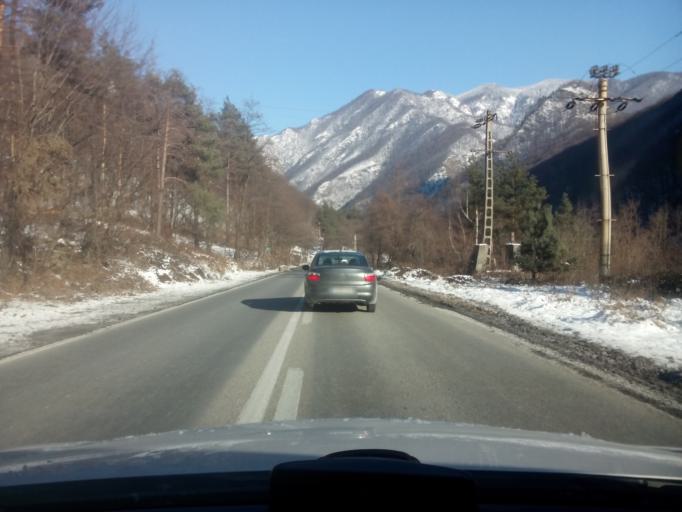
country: RO
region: Valcea
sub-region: Comuna Brezoi
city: Brezoi
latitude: 45.3115
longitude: 24.2700
